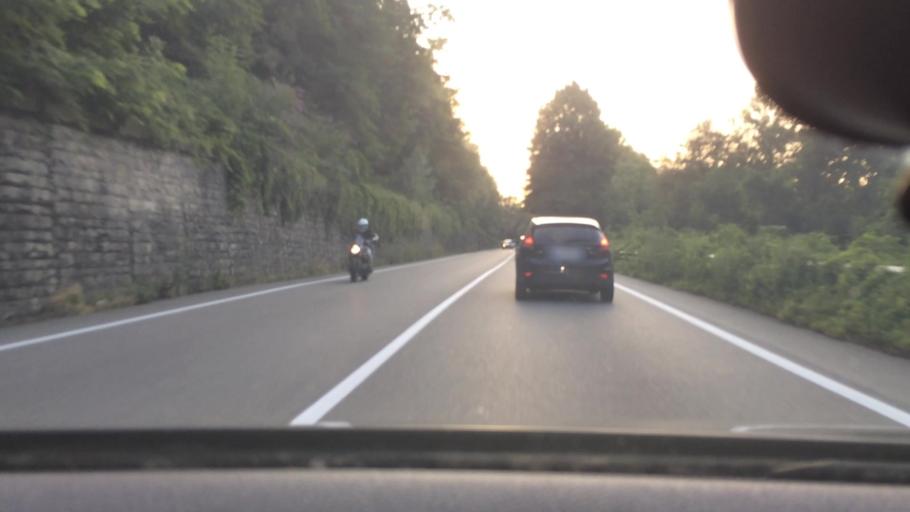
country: IT
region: Lombardy
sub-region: Provincia di Lecco
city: Cologna-Caraverio
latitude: 45.7459
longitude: 9.3447
